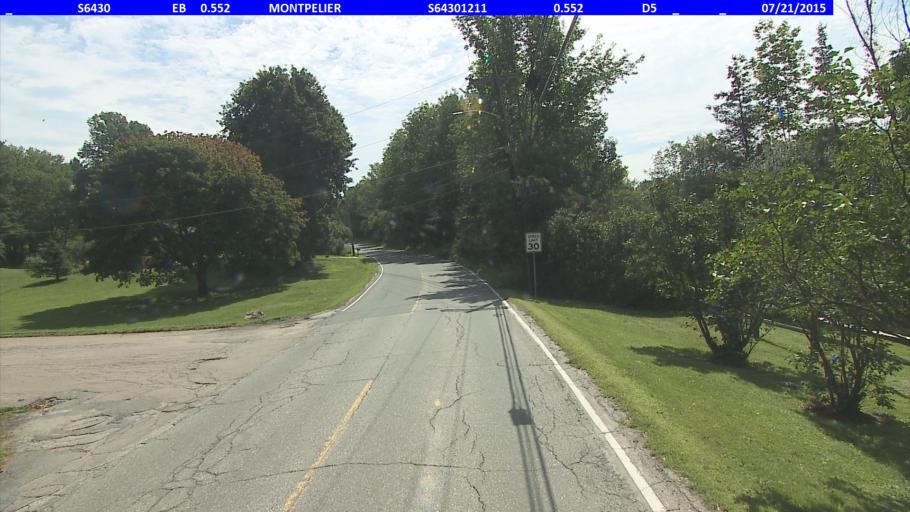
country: US
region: Vermont
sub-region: Washington County
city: Montpelier
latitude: 44.2584
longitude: -72.5489
